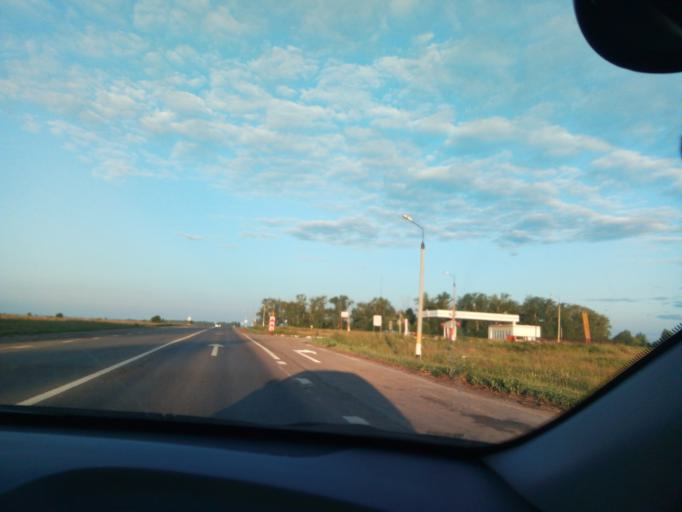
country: RU
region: Nizjnij Novgorod
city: Vyyezdnoye
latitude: 55.3395
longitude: 43.7462
